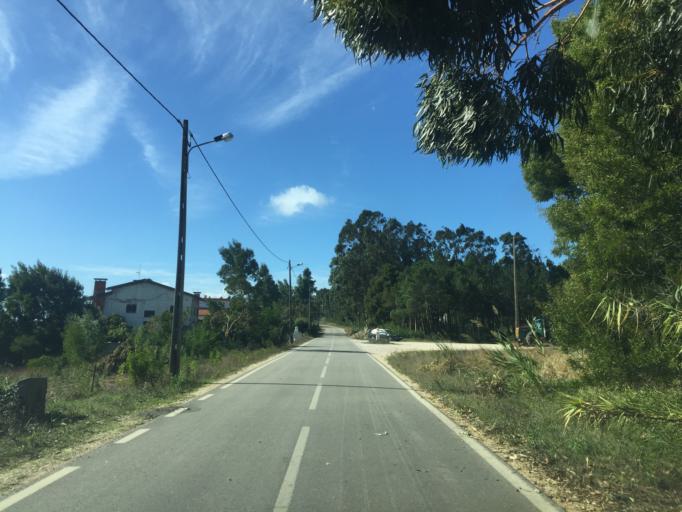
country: PT
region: Coimbra
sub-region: Figueira da Foz
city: Buarcos
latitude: 40.1916
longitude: -8.8734
